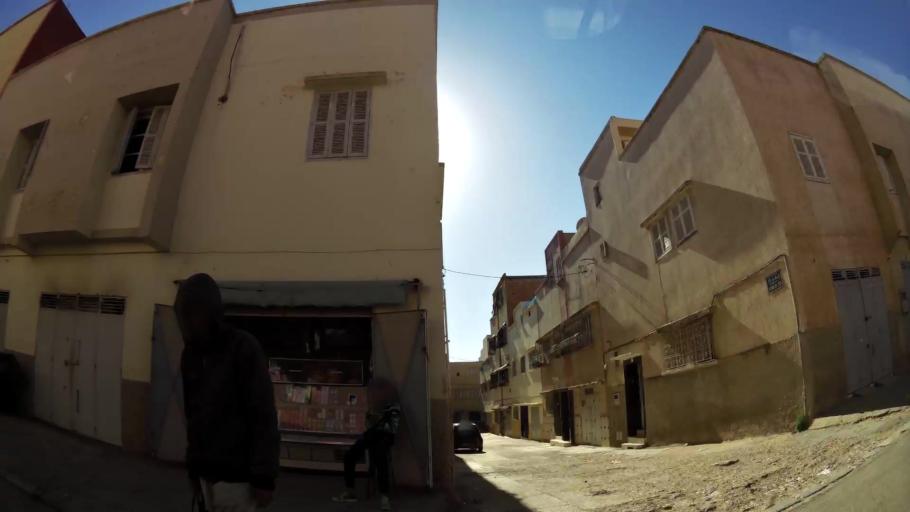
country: MA
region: Meknes-Tafilalet
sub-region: Meknes
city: Meknes
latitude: 33.8962
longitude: -5.5015
